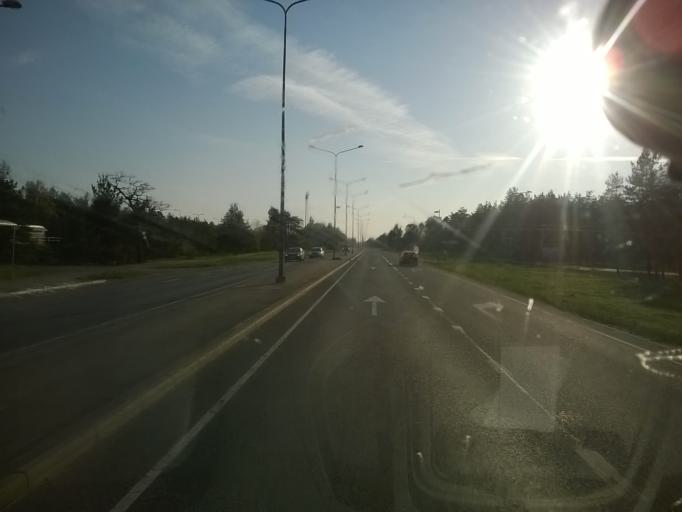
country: EE
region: Harju
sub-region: Saku vald
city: Saku
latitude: 59.3398
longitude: 24.7014
